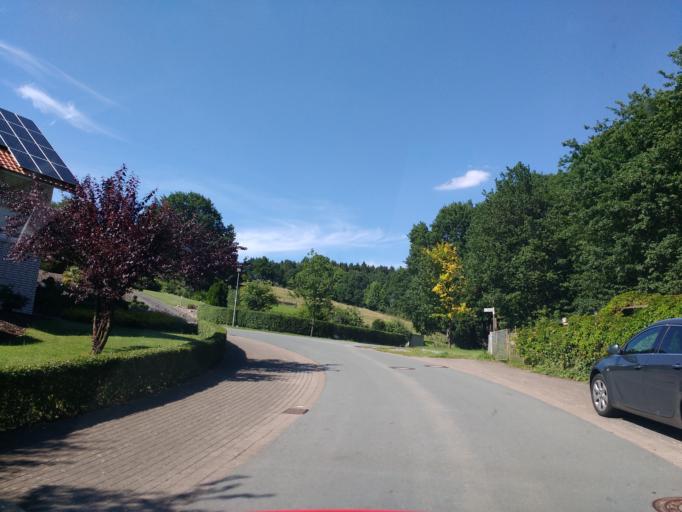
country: DE
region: North Rhine-Westphalia
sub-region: Regierungsbezirk Detmold
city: Schlangen
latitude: 51.8312
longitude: 8.8707
